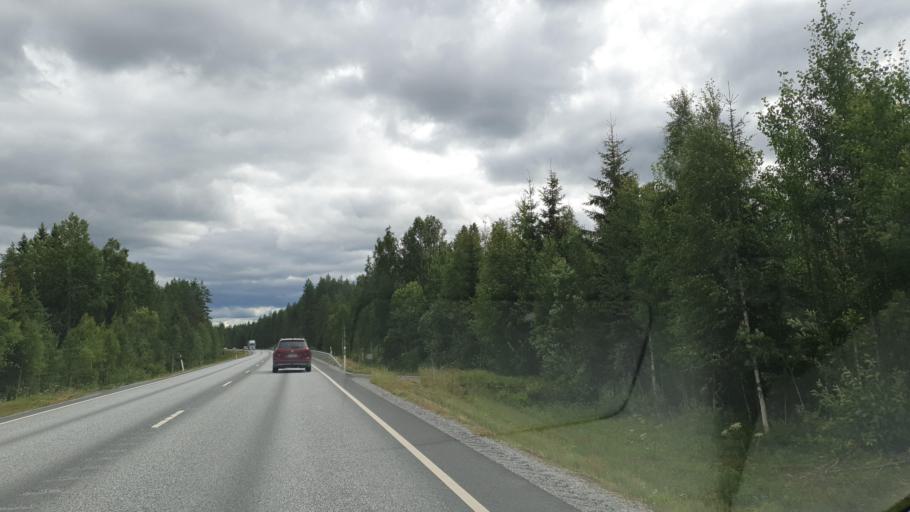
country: FI
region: Northern Savo
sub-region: Ylae-Savo
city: Sonkajaervi
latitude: 63.9118
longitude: 27.3849
